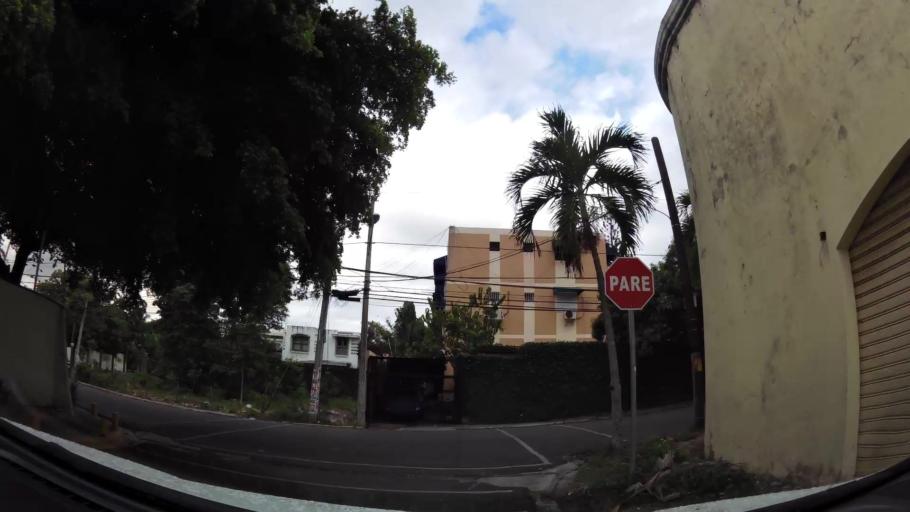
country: DO
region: Nacional
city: La Agustina
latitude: 18.4956
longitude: -69.9377
